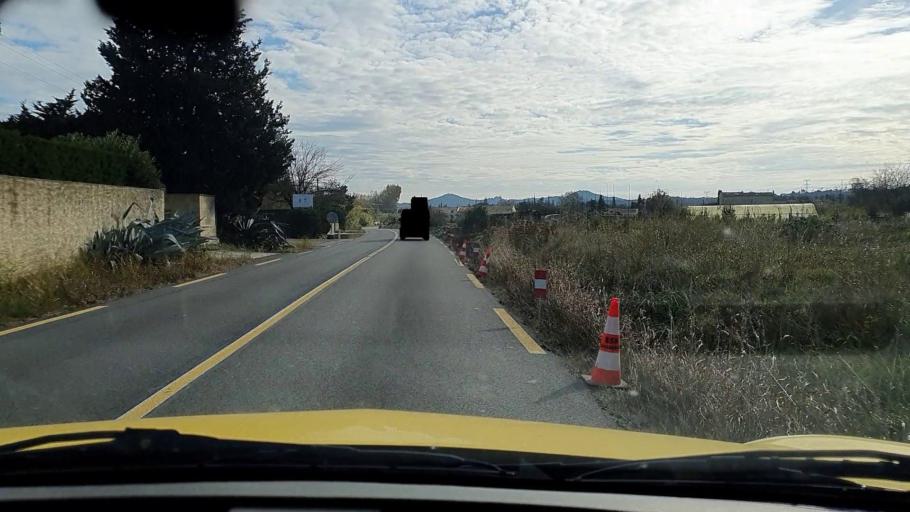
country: FR
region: Languedoc-Roussillon
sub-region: Departement du Gard
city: Montfrin
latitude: 43.8701
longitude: 4.5845
